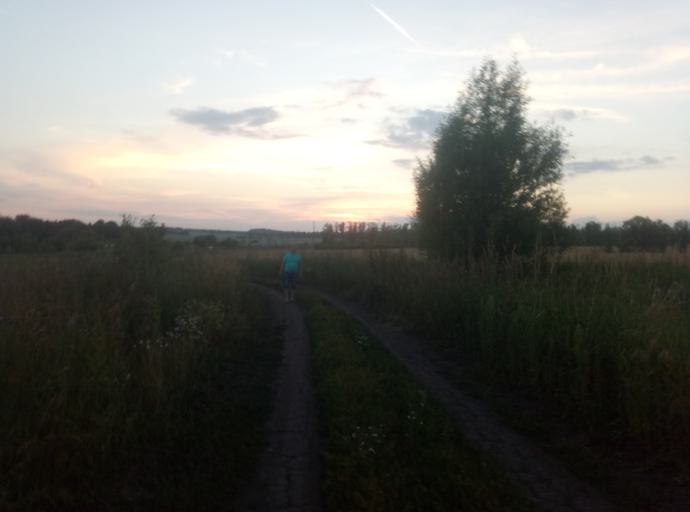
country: RU
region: Tula
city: Kireyevsk
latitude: 53.7986
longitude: 37.8680
